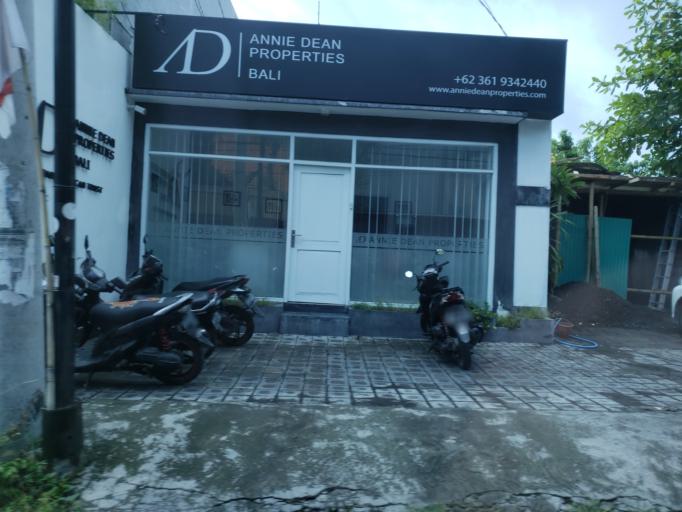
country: ID
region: Bali
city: Kuta
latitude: -8.6832
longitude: 115.1721
